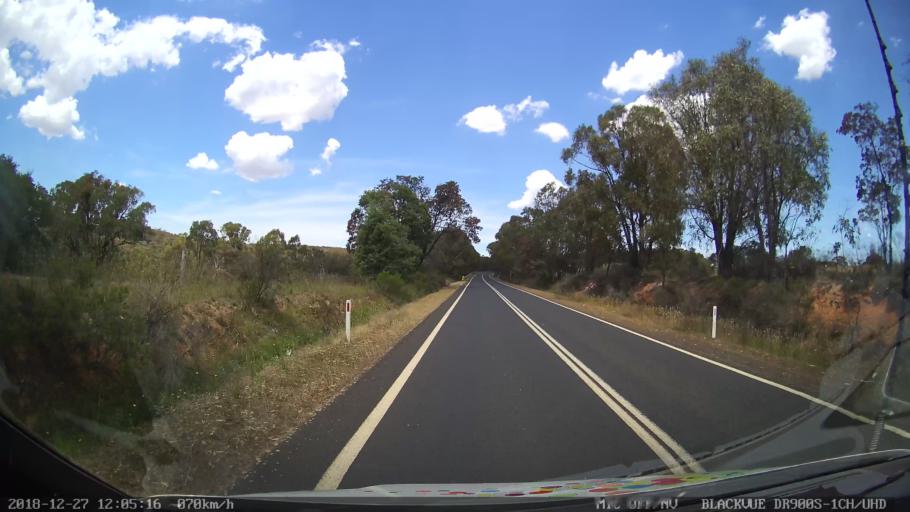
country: AU
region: New South Wales
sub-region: Blayney
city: Blayney
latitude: -33.8013
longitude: 149.3407
